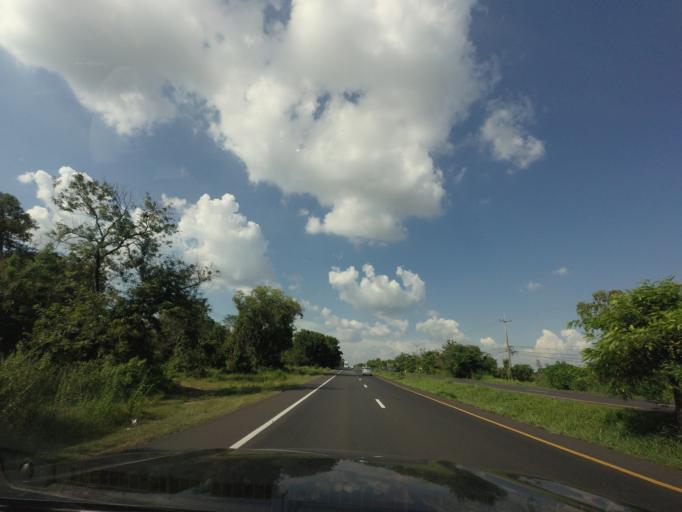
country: TH
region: Nakhon Ratchasima
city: Bua Lai
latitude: 15.6881
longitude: 102.5792
